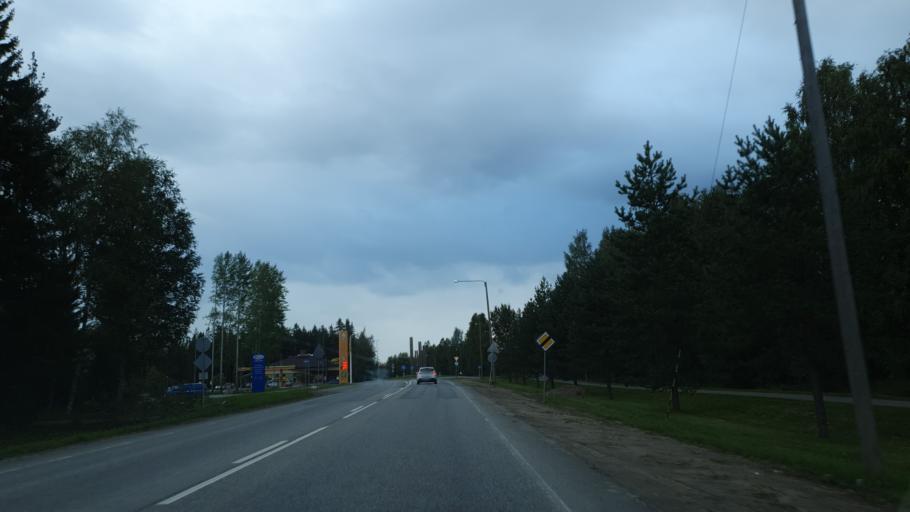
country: FI
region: North Karelia
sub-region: Pielisen Karjala
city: Lieksa
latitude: 63.3216
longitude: 30.0119
